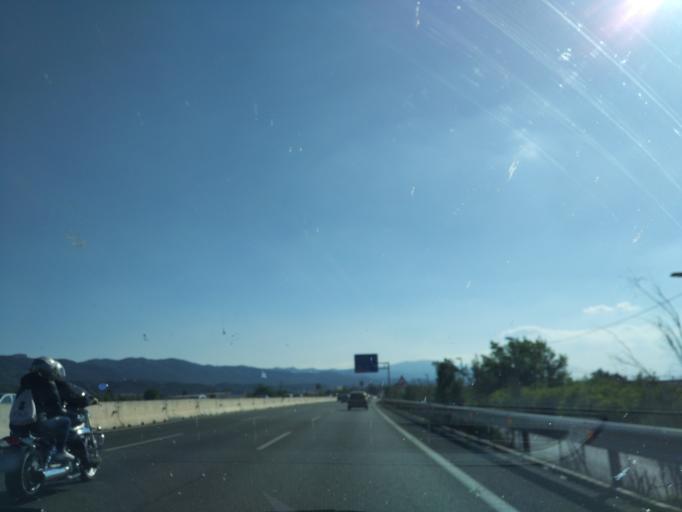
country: ES
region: Murcia
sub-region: Murcia
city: Murcia
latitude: 37.9545
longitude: -1.1392
